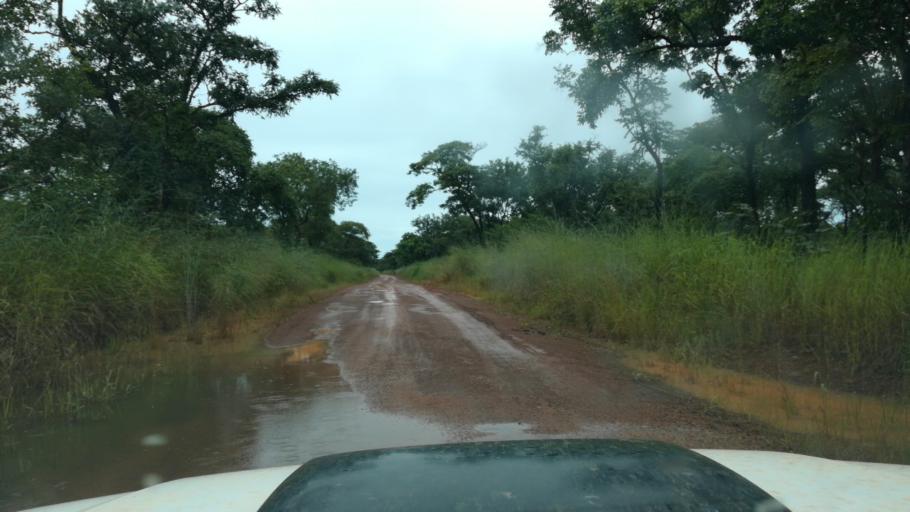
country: ZM
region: Luapula
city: Mwense
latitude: -10.1970
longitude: 28.1100
